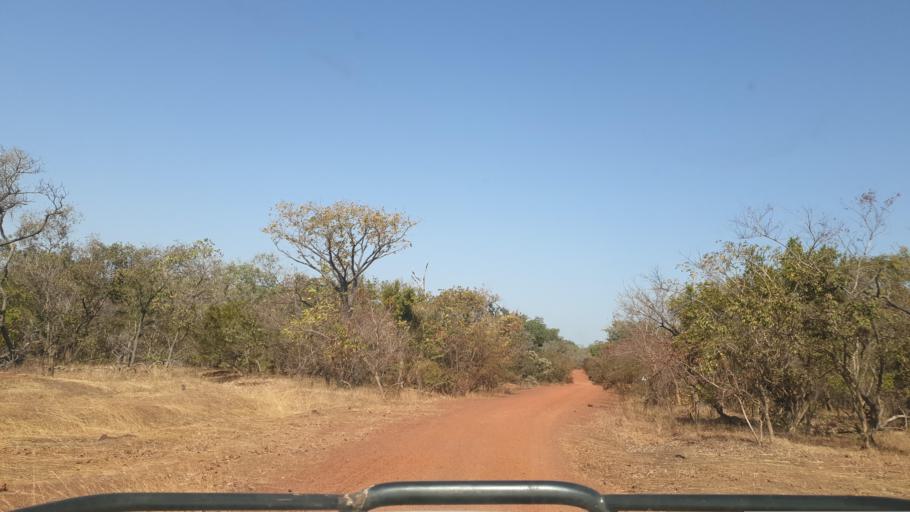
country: ML
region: Koulikoro
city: Dioila
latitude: 11.9224
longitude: -6.9839
